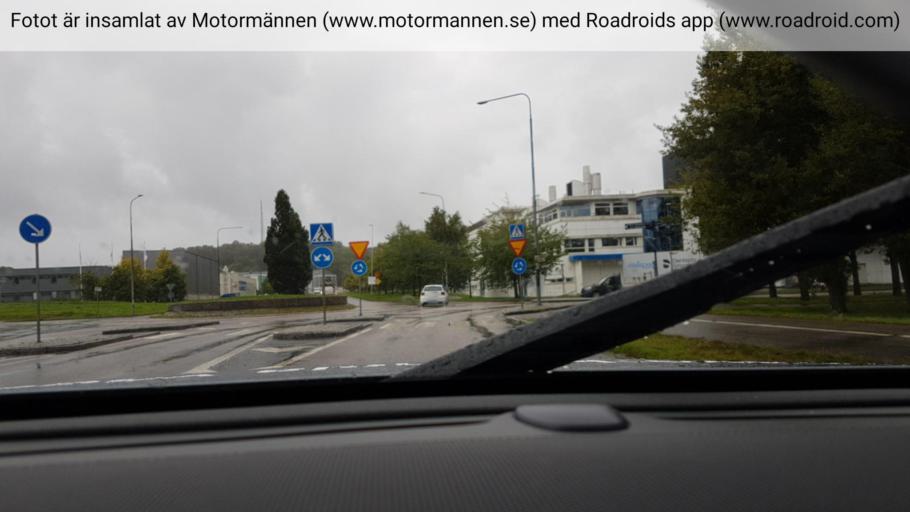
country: SE
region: Vaestra Goetaland
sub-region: Molndal
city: Moelndal
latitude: 57.6423
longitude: 12.0182
